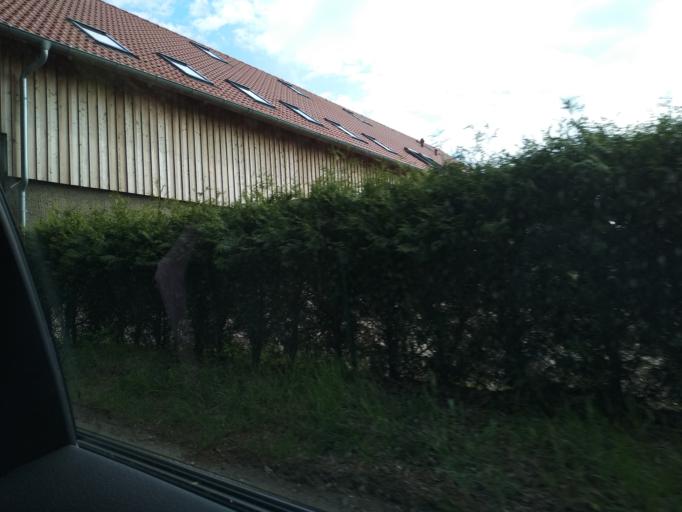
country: DE
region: Saxony
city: Stadt Wehlen
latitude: 50.9587
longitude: 14.0174
